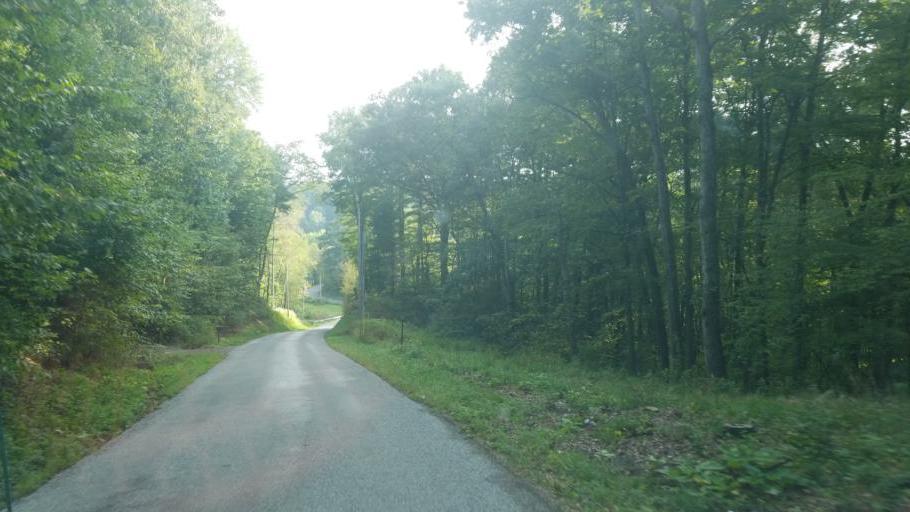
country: US
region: Ohio
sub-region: Wayne County
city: Wooster
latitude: 40.8741
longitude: -82.0238
